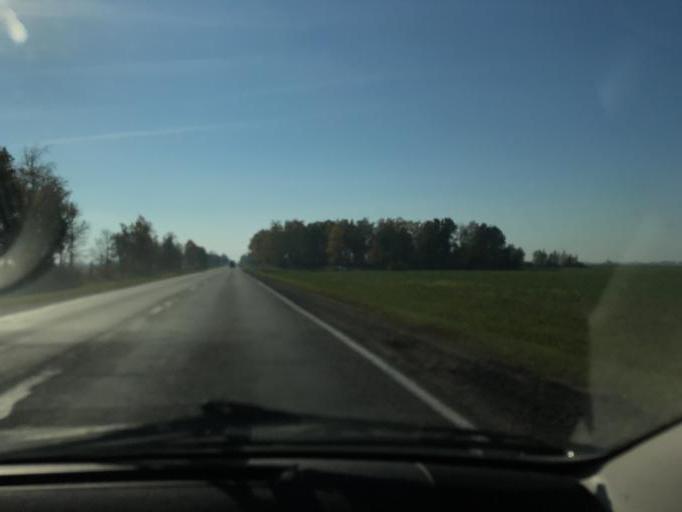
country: BY
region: Minsk
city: Salihorsk
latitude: 52.9109
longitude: 27.4795
